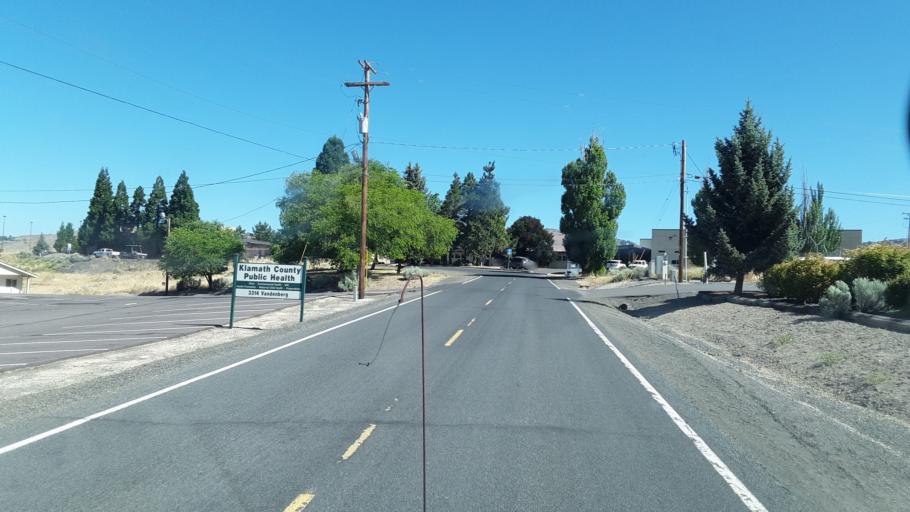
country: US
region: Oregon
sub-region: Klamath County
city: Altamont
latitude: 42.2207
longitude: -121.7482
